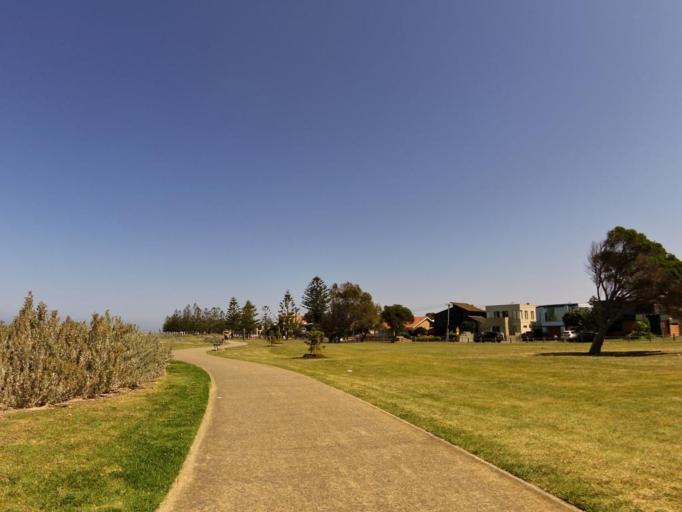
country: AU
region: Victoria
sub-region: Hobsons Bay
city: Seaholme
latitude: -37.8684
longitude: 144.8443
